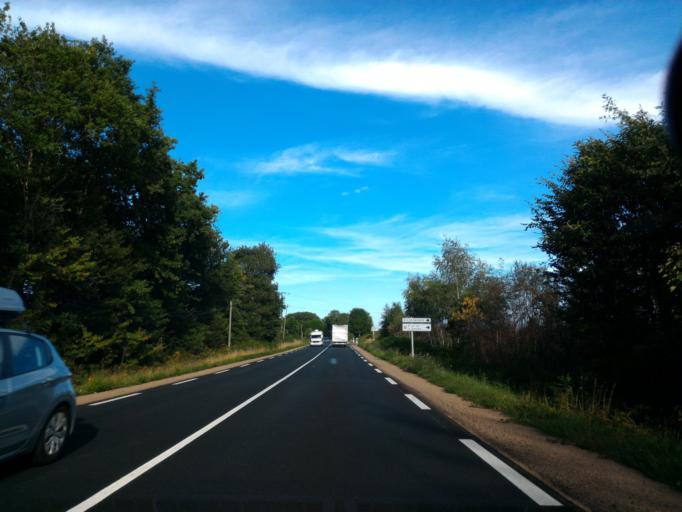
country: FR
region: Limousin
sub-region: Departement de la Haute-Vienne
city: Magnac-Laval
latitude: 46.1838
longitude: 1.1884
